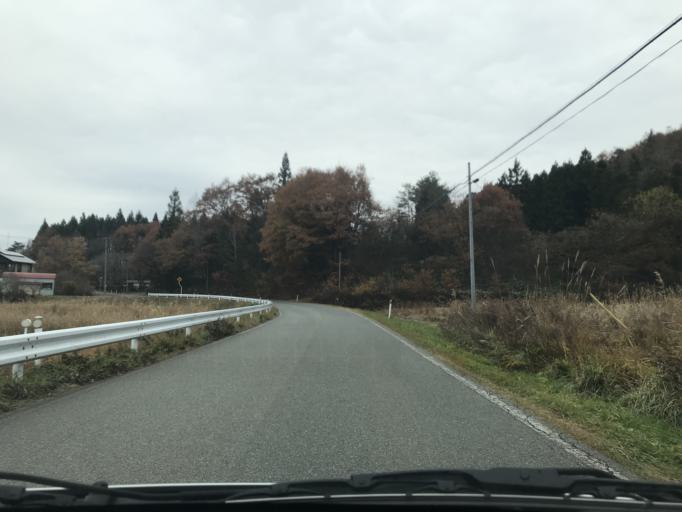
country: JP
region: Iwate
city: Kitakami
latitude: 39.2846
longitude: 141.1777
